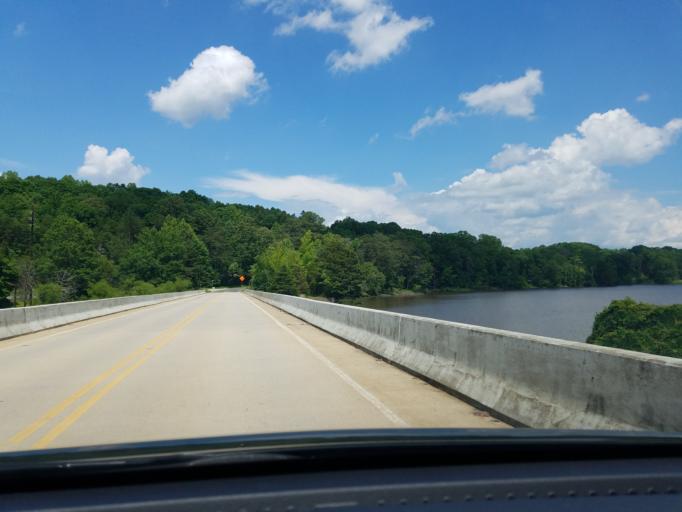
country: US
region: North Carolina
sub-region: Granville County
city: Butner
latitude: 36.1737
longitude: -78.8633
